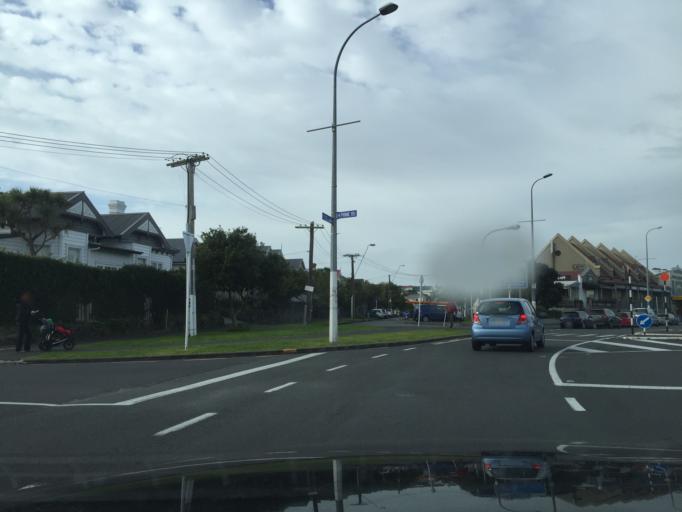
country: NZ
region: Auckland
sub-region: Auckland
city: Auckland
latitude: -36.8634
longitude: 174.7371
